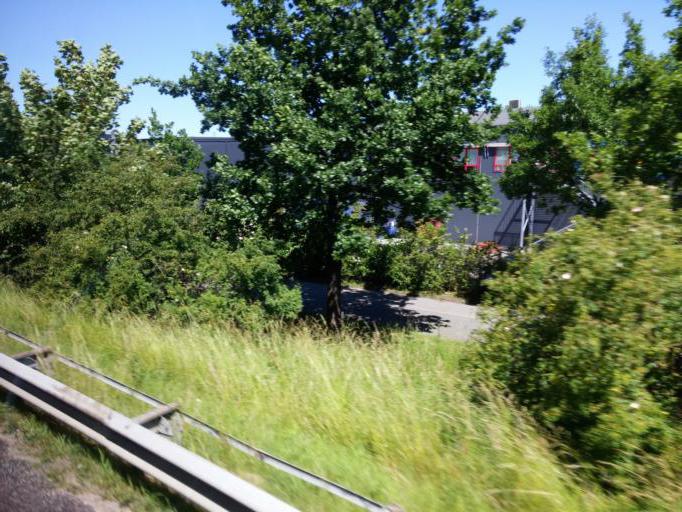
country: SE
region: Skane
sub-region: Malmo
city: Oxie
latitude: 55.5663
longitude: 13.0613
